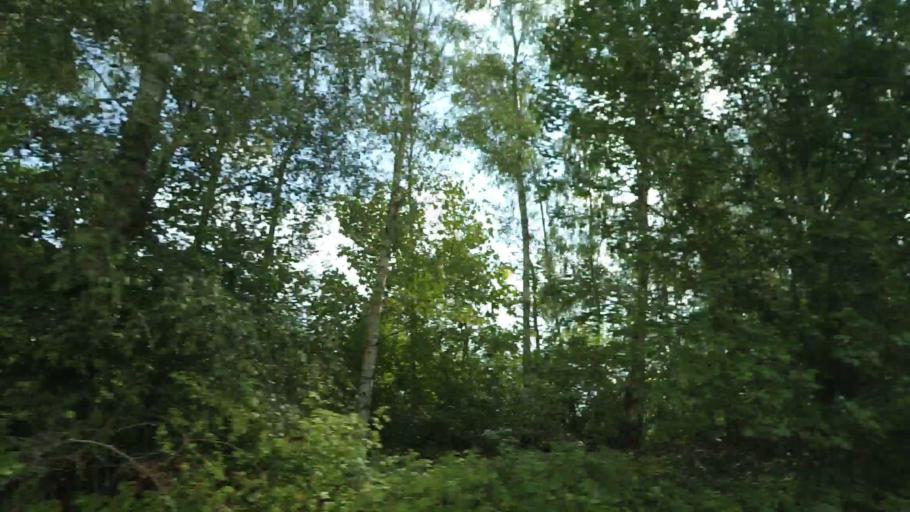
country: DK
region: Central Jutland
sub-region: Norddjurs Kommune
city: Allingabro
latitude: 56.5433
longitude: 10.3630
